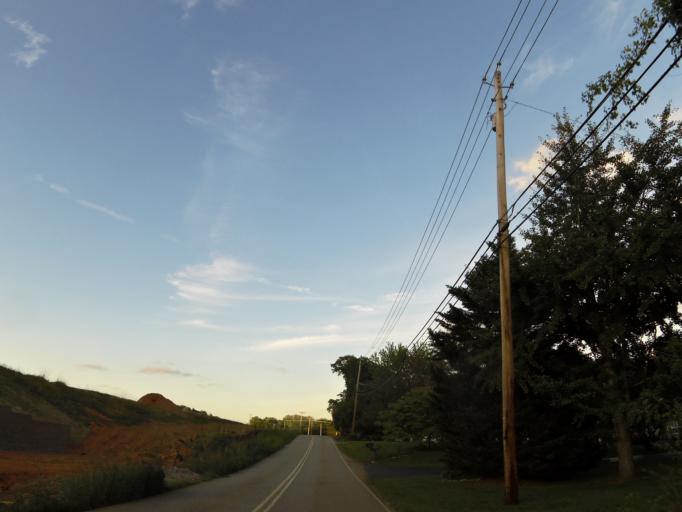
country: US
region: Tennessee
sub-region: Knox County
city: Farragut
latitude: 35.9236
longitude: -84.1520
